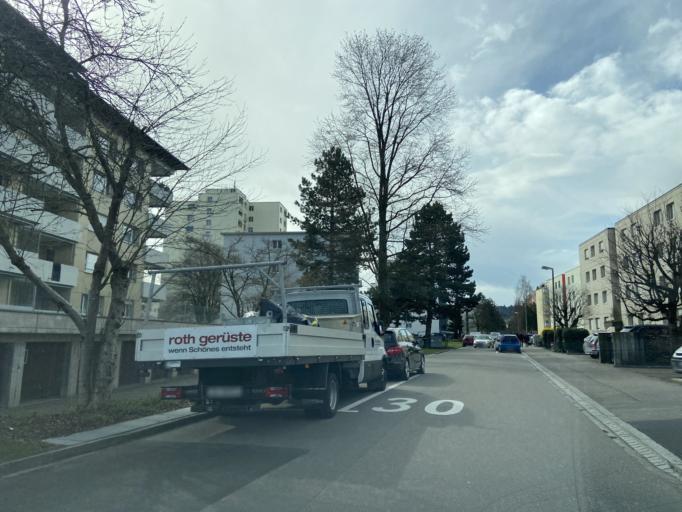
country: CH
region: Zurich
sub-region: Bezirk Winterthur
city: Seen (Kreis 3) / Waser
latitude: 47.4913
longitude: 8.7616
